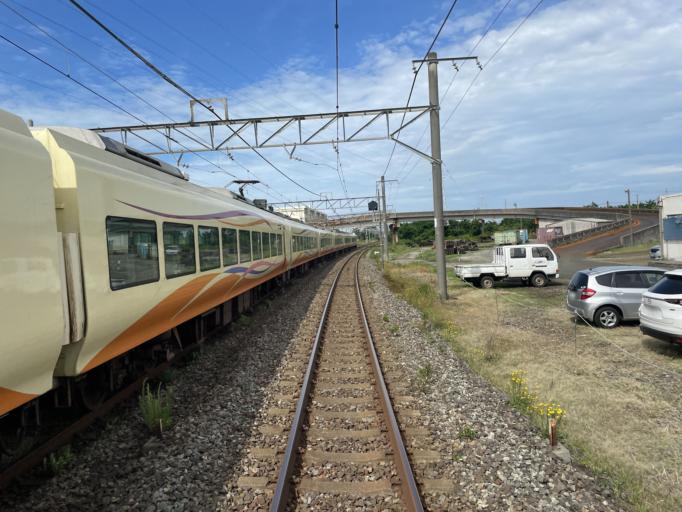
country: JP
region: Niigata
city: Kameda-honcho
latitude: 37.9054
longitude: 139.0998
